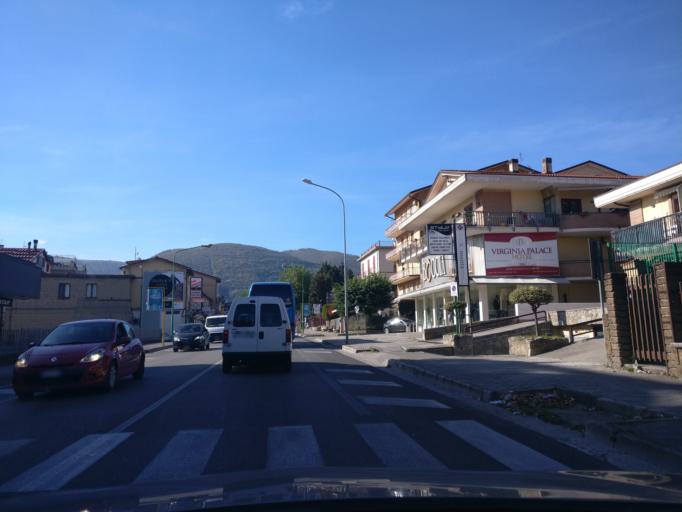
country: IT
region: Campania
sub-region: Provincia di Avellino
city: Torelli-Torrette
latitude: 40.9068
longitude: 14.7597
